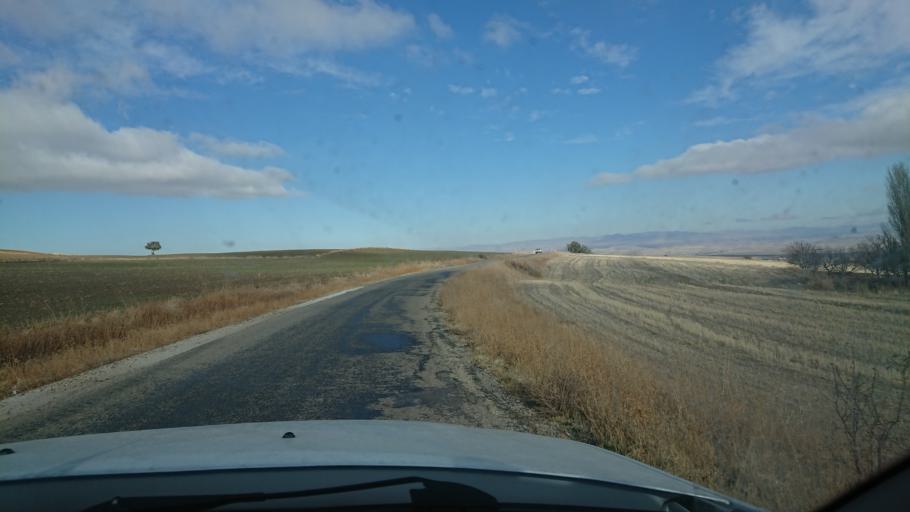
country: TR
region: Aksaray
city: Agacoren
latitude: 38.8451
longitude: 33.9495
